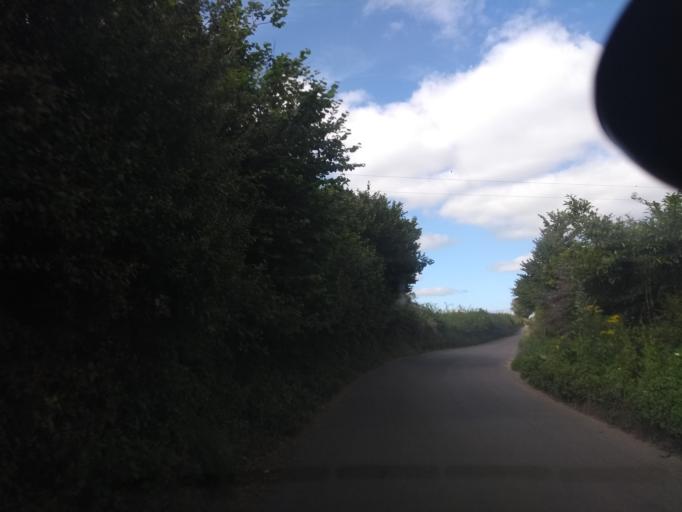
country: GB
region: England
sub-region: Devon
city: Modbury
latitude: 50.3064
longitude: -3.8851
